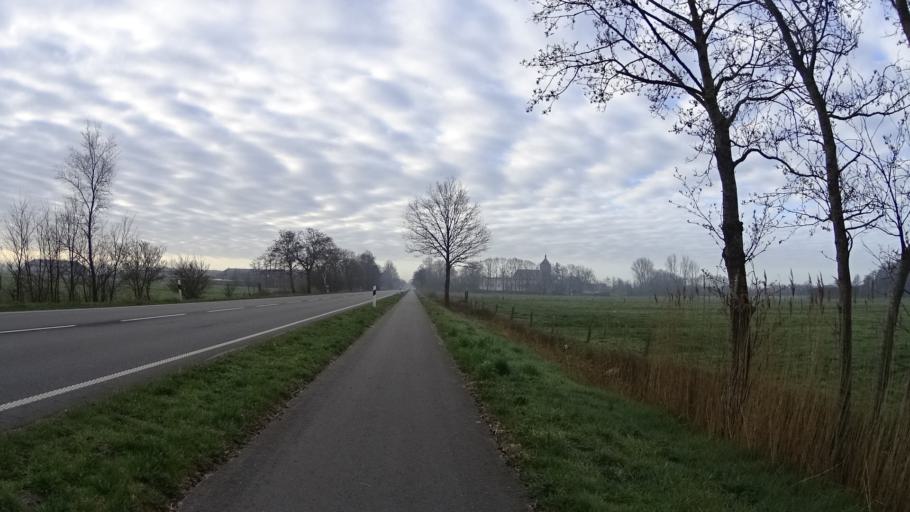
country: DE
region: Lower Saxony
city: Osteel
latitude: 53.5383
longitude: 7.2623
